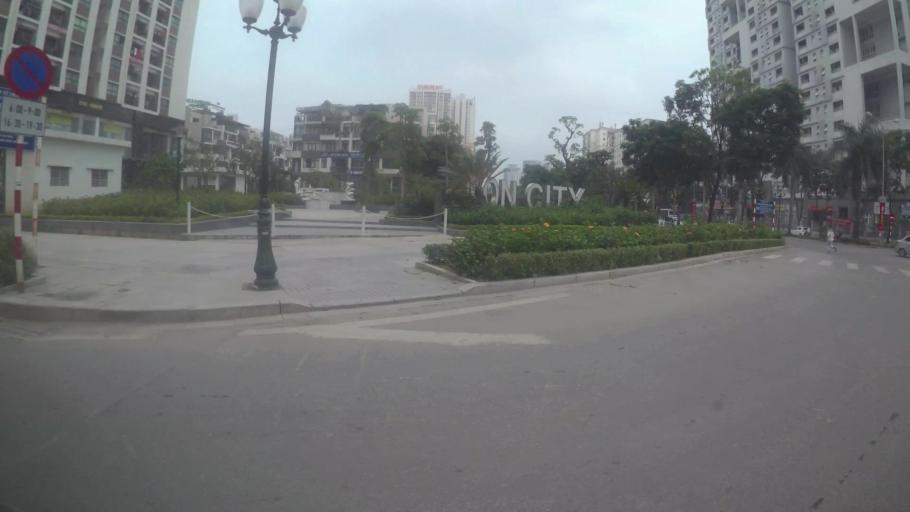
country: VN
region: Ha Noi
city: Cau Dien
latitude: 21.0348
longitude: 105.7662
